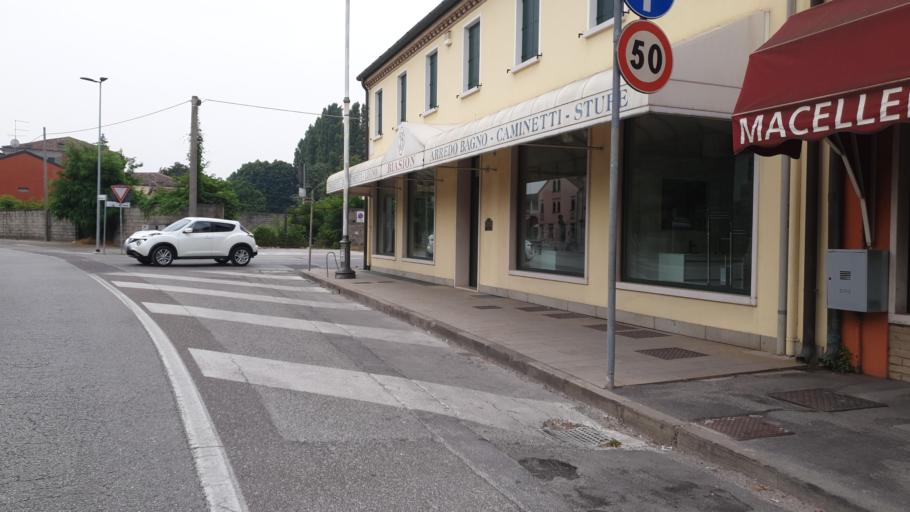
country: IT
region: Veneto
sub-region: Provincia di Padova
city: Piove di Sacco-Piovega
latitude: 45.2904
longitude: 12.0311
